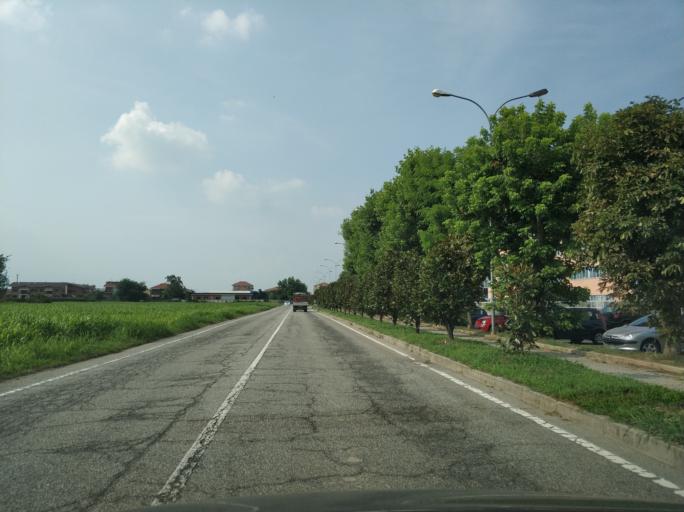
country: IT
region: Piedmont
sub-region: Provincia di Torino
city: Leini
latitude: 45.1778
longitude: 7.7095
